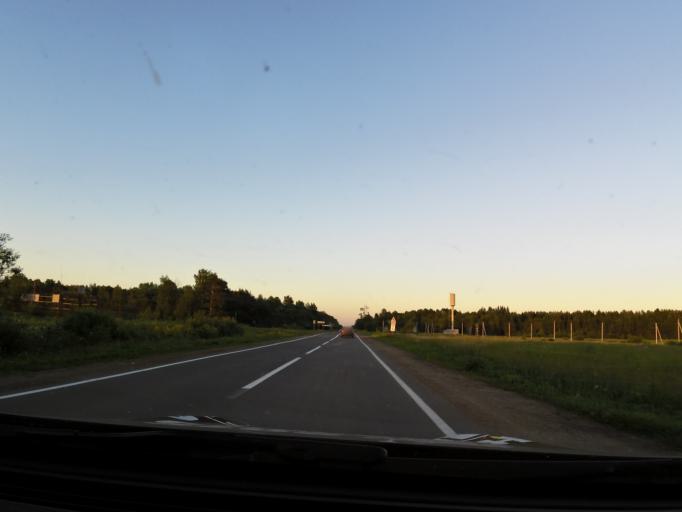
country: RU
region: Jaroslavl
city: Lyubim
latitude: 58.3584
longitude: 40.5564
